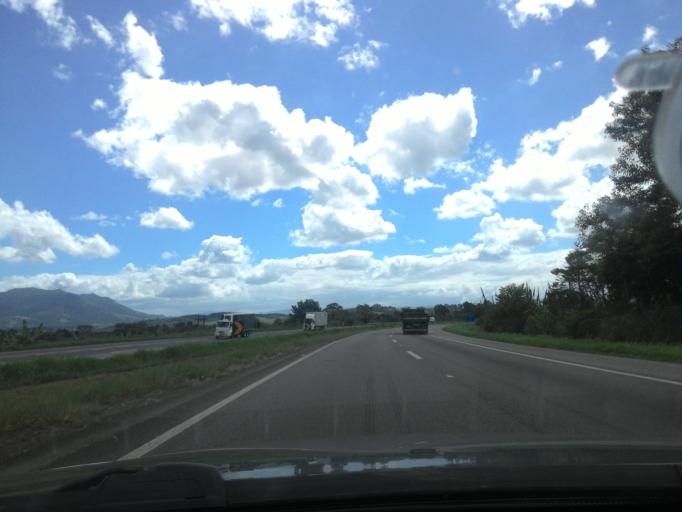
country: BR
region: Sao Paulo
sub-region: Jacupiranga
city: Jacupiranga
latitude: -24.7226
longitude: -48.0454
